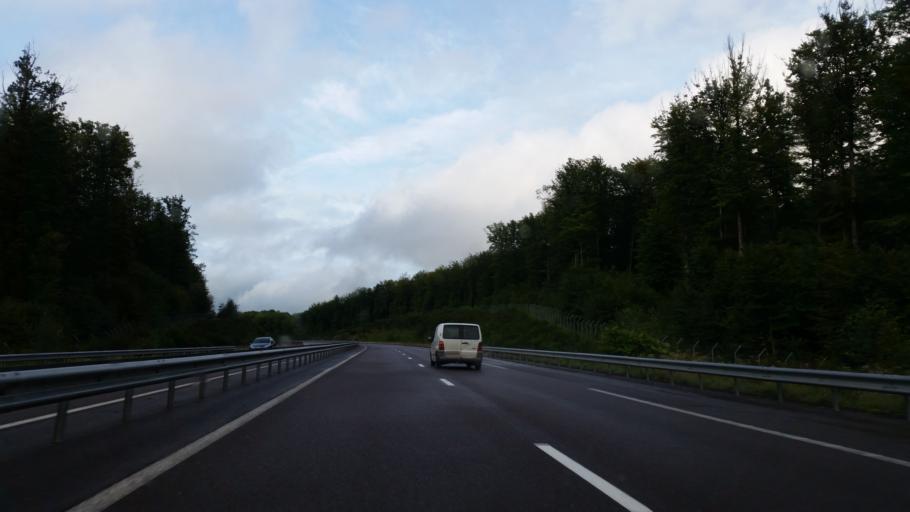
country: FR
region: Franche-Comte
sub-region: Departement de la Haute-Saone
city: Froideconche
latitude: 47.8284
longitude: 6.4002
